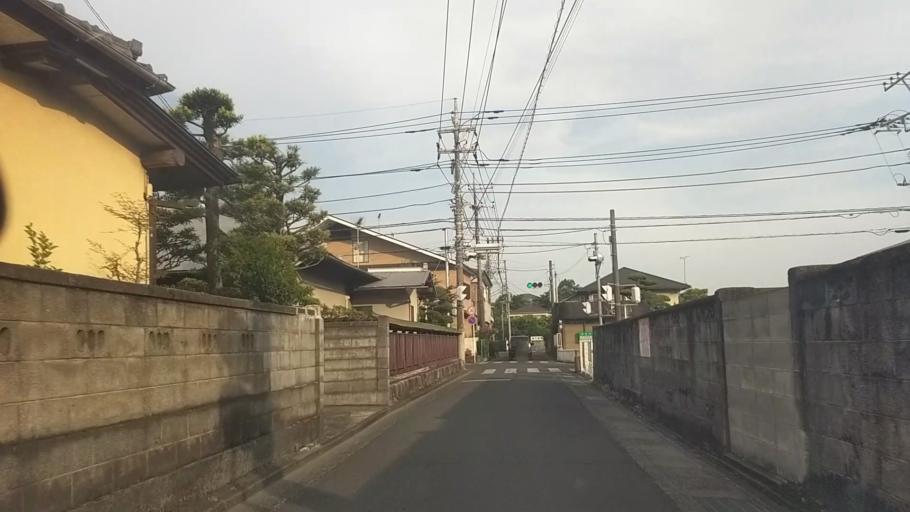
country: JP
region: Kanagawa
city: Odawara
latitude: 35.3150
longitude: 139.1168
